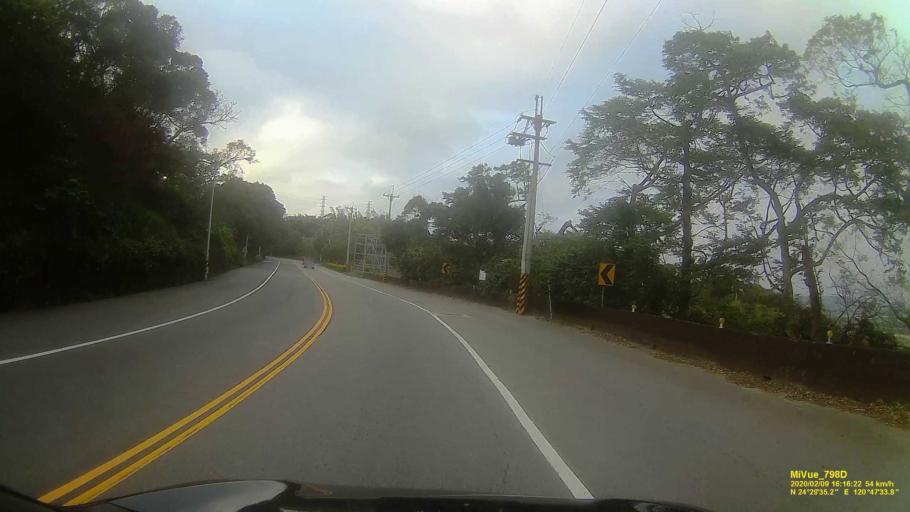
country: TW
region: Taiwan
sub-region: Miaoli
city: Miaoli
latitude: 24.4934
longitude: 120.7926
